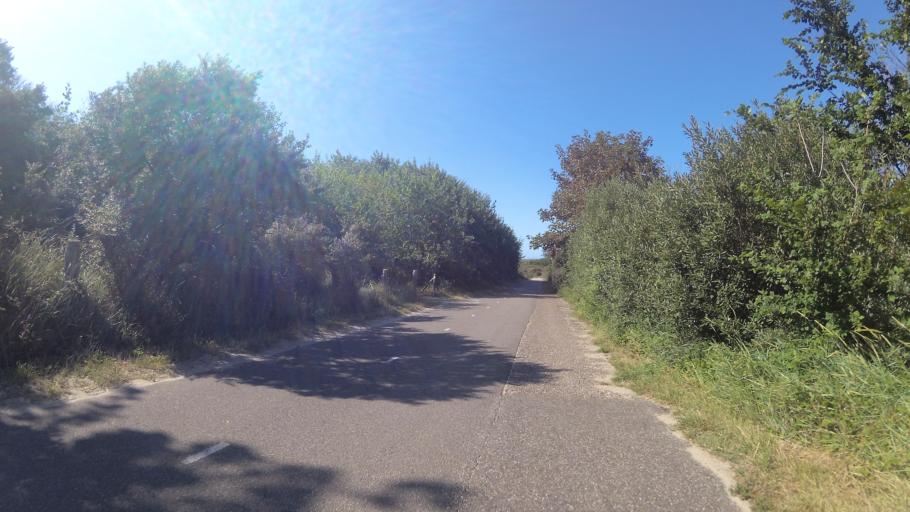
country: NL
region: Zeeland
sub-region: Gemeente Vlissingen
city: Vlissingen
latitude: 51.5186
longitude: 3.4489
